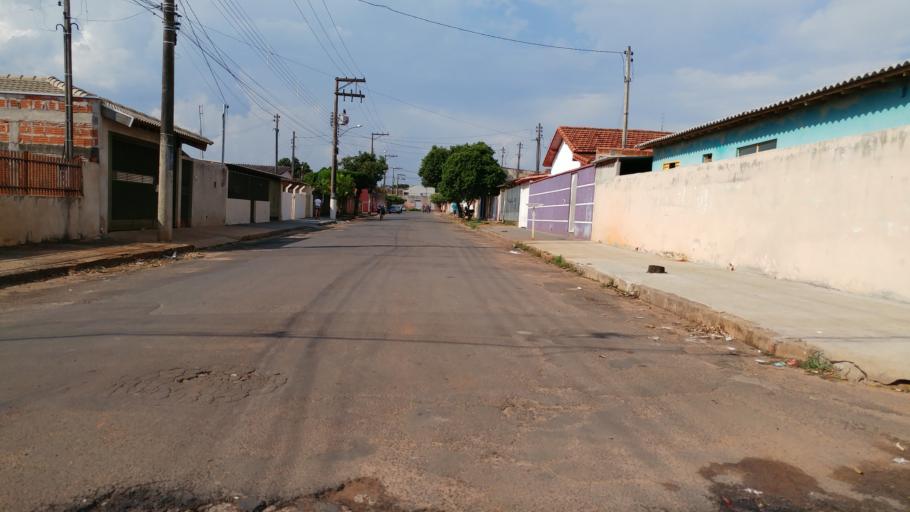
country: BR
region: Sao Paulo
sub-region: Paraguacu Paulista
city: Paraguacu Paulista
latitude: -22.4227
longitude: -50.5866
